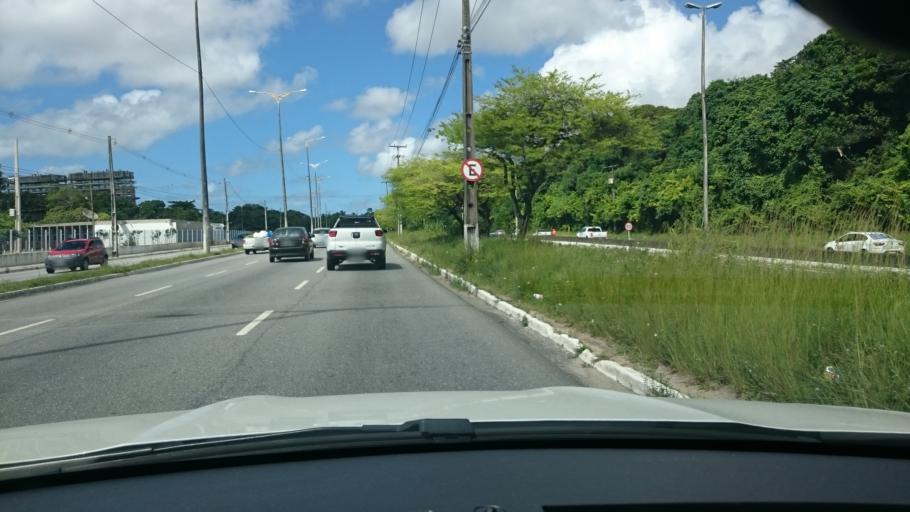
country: BR
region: Paraiba
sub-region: Joao Pessoa
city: Joao Pessoa
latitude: -7.1428
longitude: -34.8514
